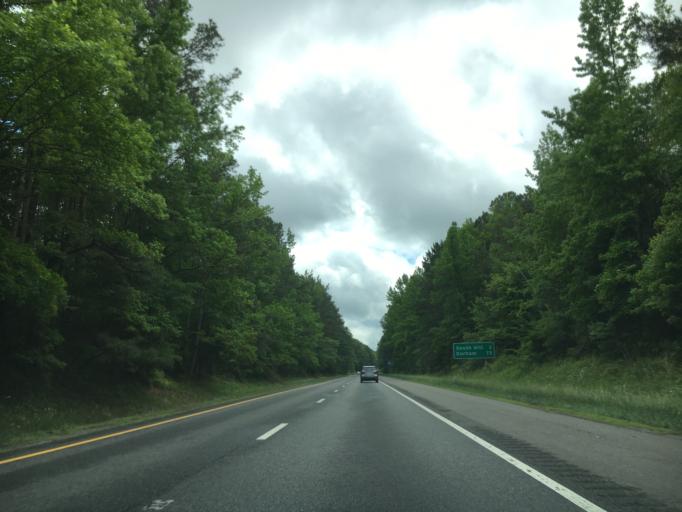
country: US
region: Virginia
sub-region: Mecklenburg County
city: South Hill
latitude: 36.7381
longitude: -78.1011
